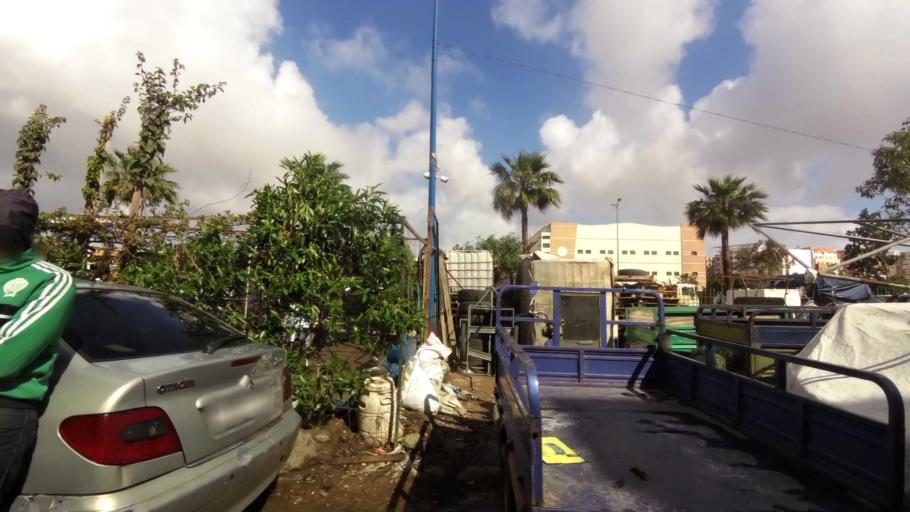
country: MA
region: Grand Casablanca
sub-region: Nouaceur
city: Bouskoura
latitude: 33.5293
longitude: -7.6771
